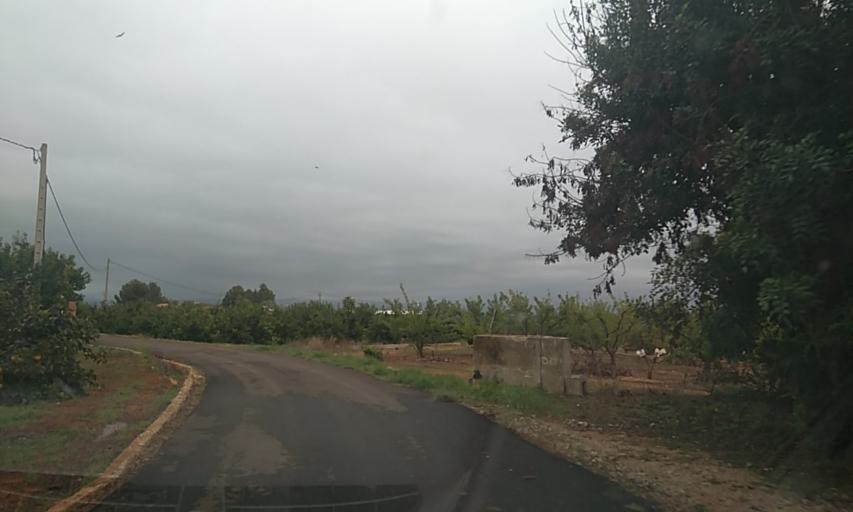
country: ES
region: Valencia
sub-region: Provincia de Valencia
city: Benimodo
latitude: 39.1920
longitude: -0.5595
